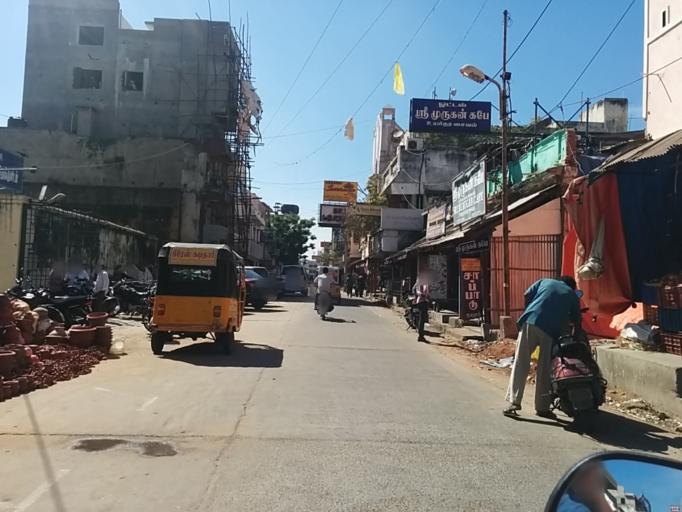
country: IN
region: Pondicherry
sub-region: Puducherry
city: Puducherry
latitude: 11.9370
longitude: 79.8285
